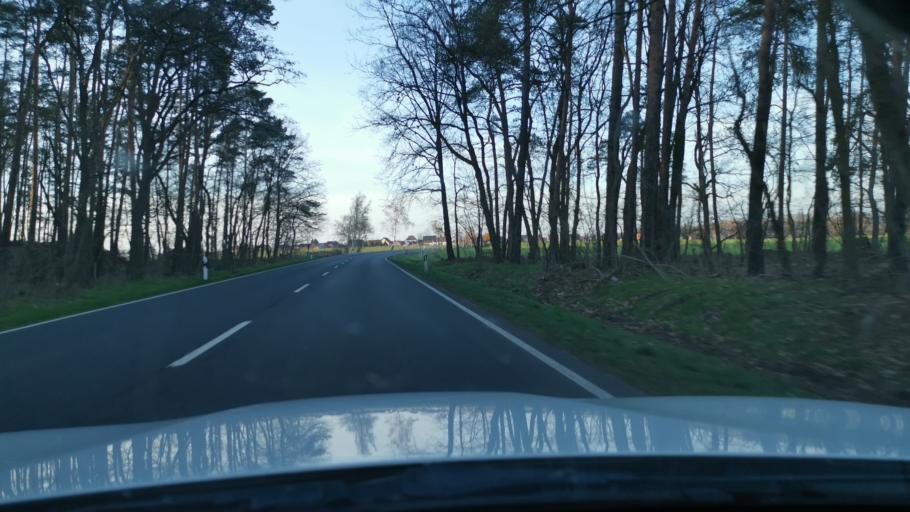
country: DE
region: Saxony
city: Bad Duben
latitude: 51.6289
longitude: 12.5882
